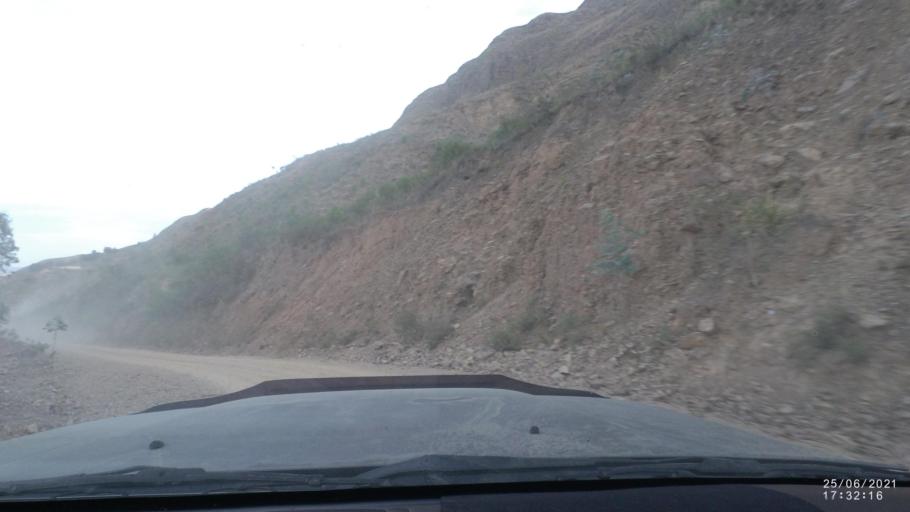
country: BO
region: Cochabamba
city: Mizque
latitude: -17.9402
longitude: -65.6635
